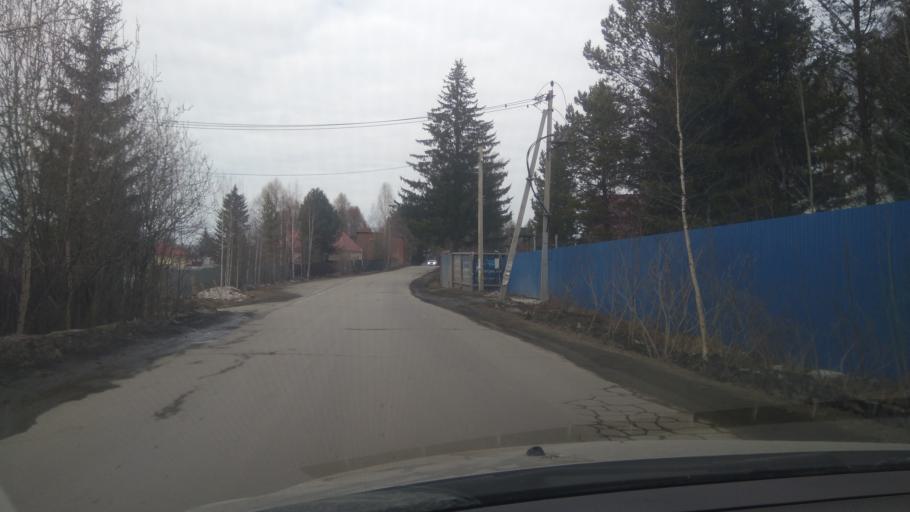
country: RU
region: Sverdlovsk
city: Severka
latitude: 56.8455
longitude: 60.3833
